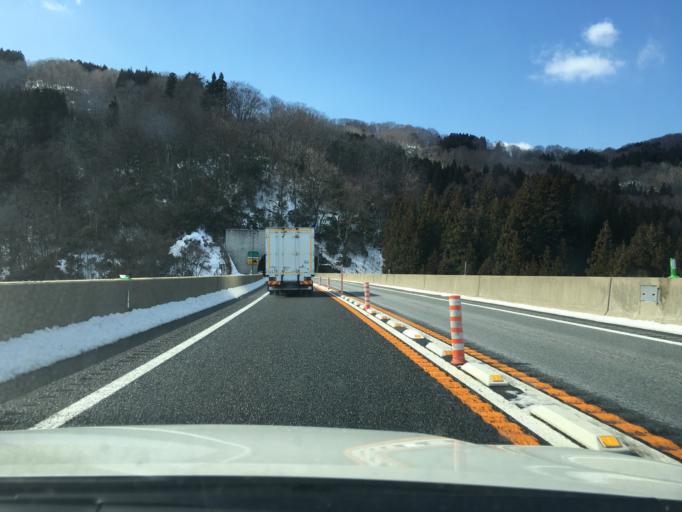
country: JP
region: Yamagata
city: Tsuruoka
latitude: 38.5929
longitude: 139.8828
